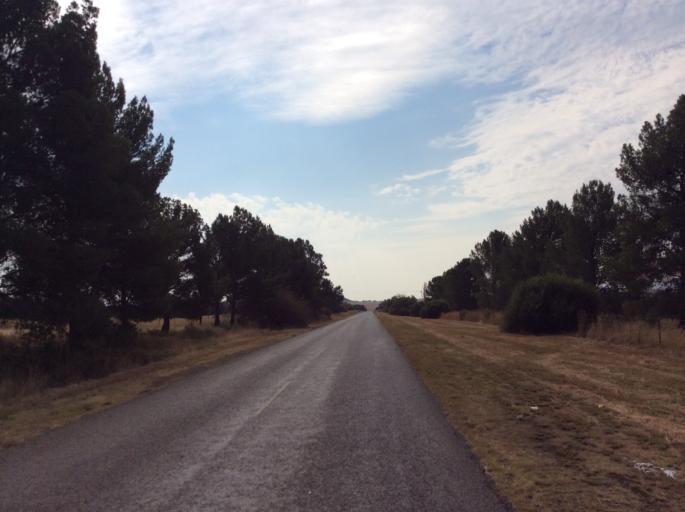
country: ZA
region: Orange Free State
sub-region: Xhariep District Municipality
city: Dewetsdorp
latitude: -29.5679
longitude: 26.6659
